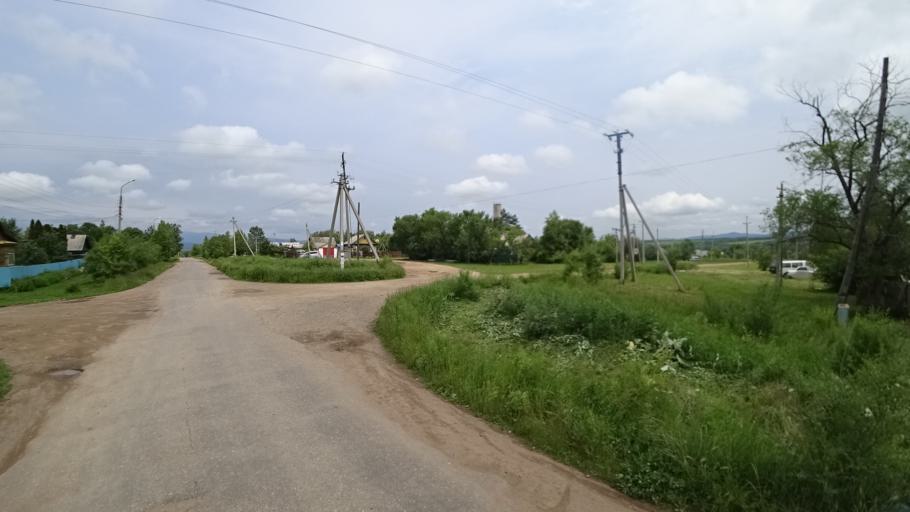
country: RU
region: Primorskiy
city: Novosysoyevka
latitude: 44.2322
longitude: 133.3601
